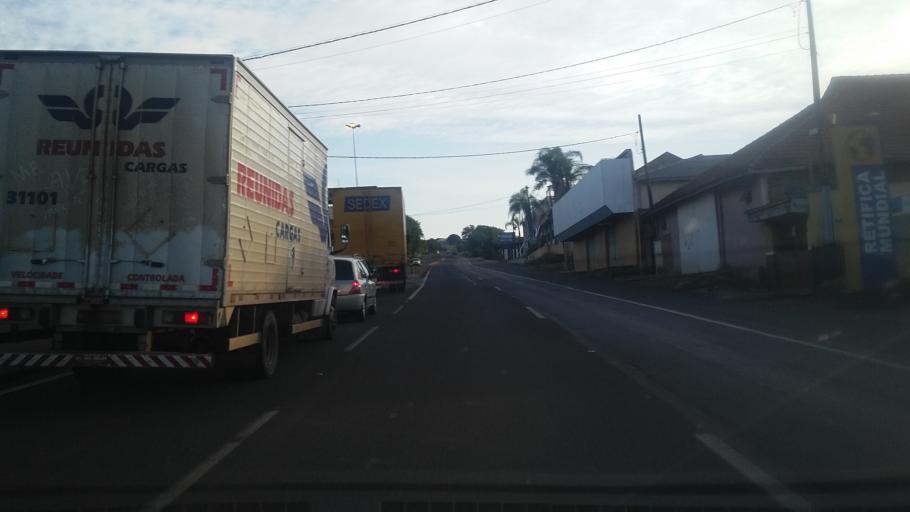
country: BR
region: Parana
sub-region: Assai
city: Assai
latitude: -23.1945
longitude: -50.6517
